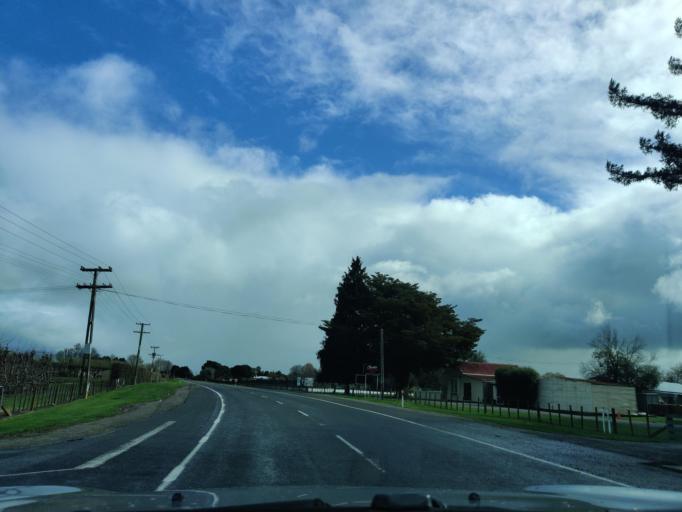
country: NZ
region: Hawke's Bay
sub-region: Hastings District
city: Hastings
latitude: -39.6783
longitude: 176.8490
